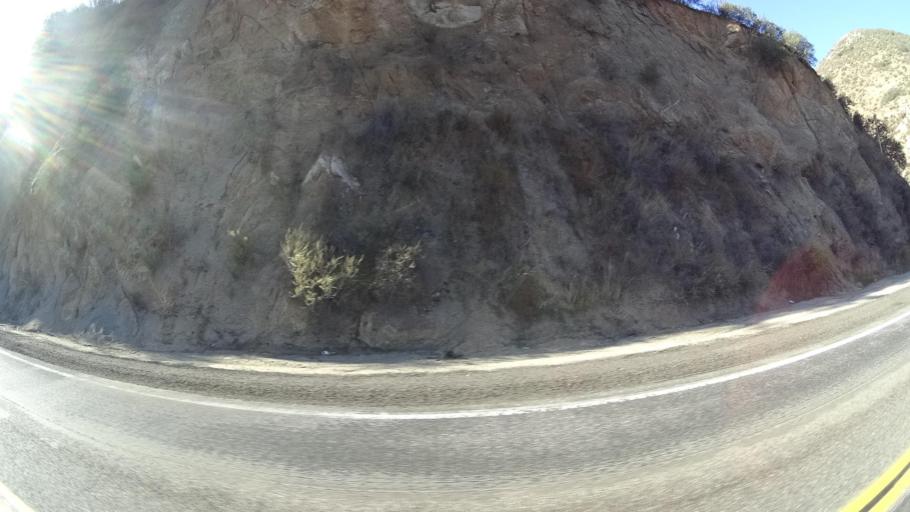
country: MX
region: Baja California
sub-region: Tecate
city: Lomas de Santa Anita
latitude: 32.5973
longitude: -116.6796
